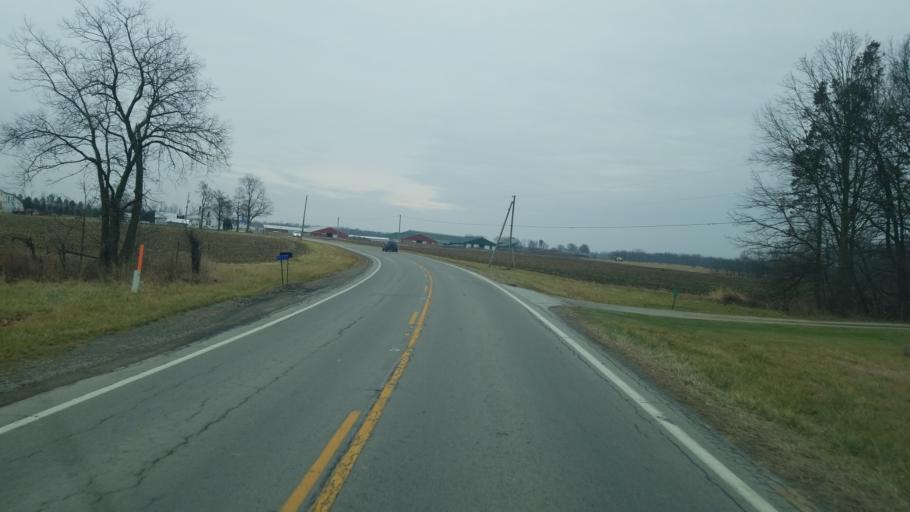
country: US
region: Ohio
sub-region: Hardin County
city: Forest
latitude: 40.6981
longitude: -83.4211
